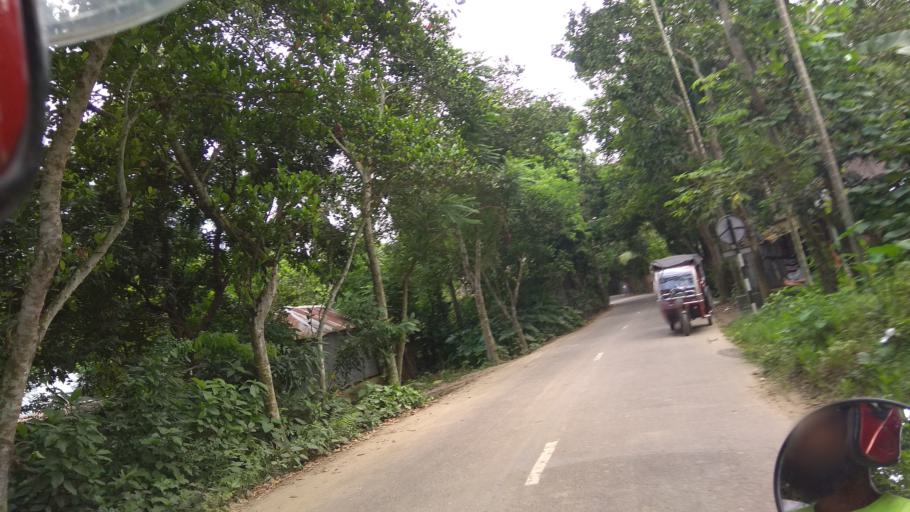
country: BD
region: Khulna
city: Kalia
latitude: 23.1646
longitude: 89.6450
